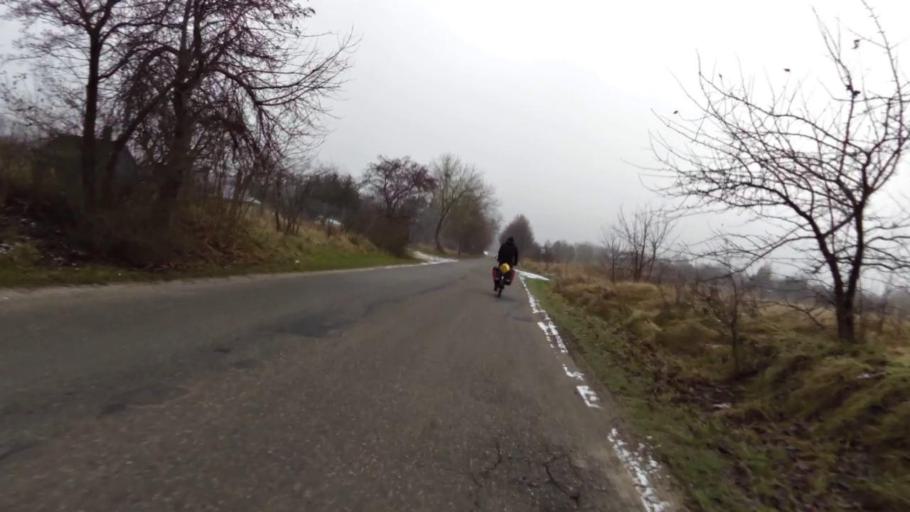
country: PL
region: West Pomeranian Voivodeship
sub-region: Powiat walecki
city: Walcz
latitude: 53.2883
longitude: 16.4743
